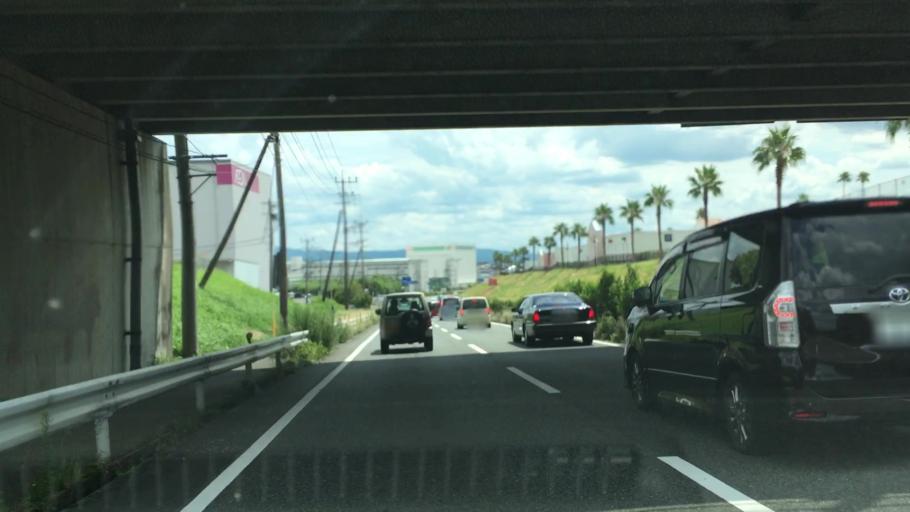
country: JP
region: Saga Prefecture
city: Tosu
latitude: 33.4091
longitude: 130.5115
